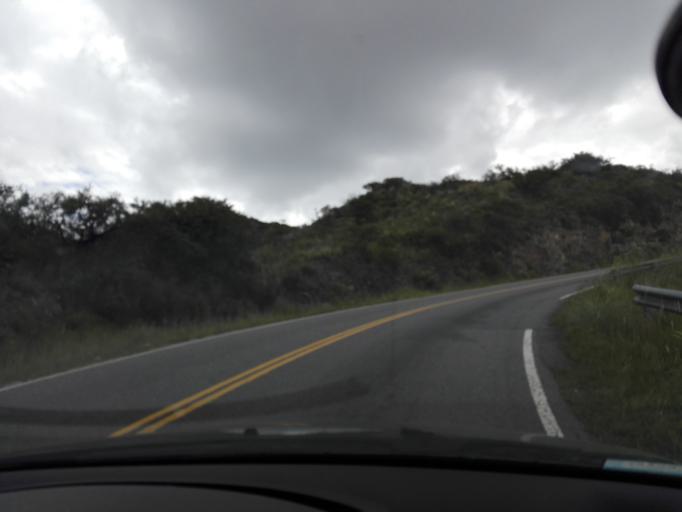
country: AR
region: Cordoba
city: Cuesta Blanca
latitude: -31.5943
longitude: -64.5292
